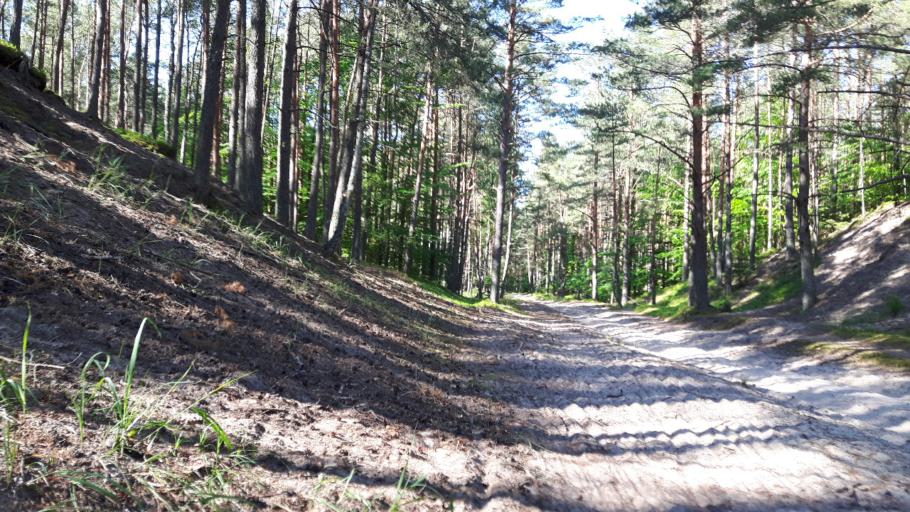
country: PL
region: Pomeranian Voivodeship
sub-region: Powiat leborski
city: Leba
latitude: 54.7061
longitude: 17.5245
